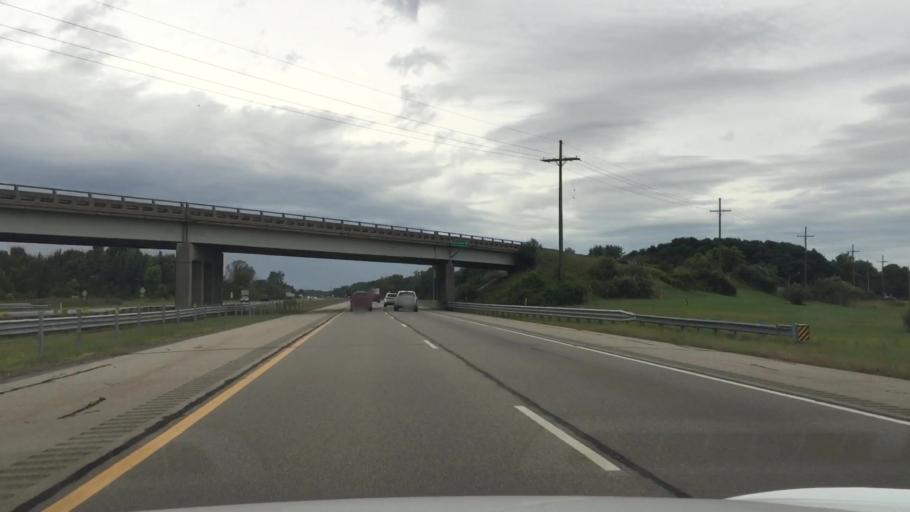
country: US
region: Michigan
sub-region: Macomb County
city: New Baltimore
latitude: 42.7207
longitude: -82.7531
